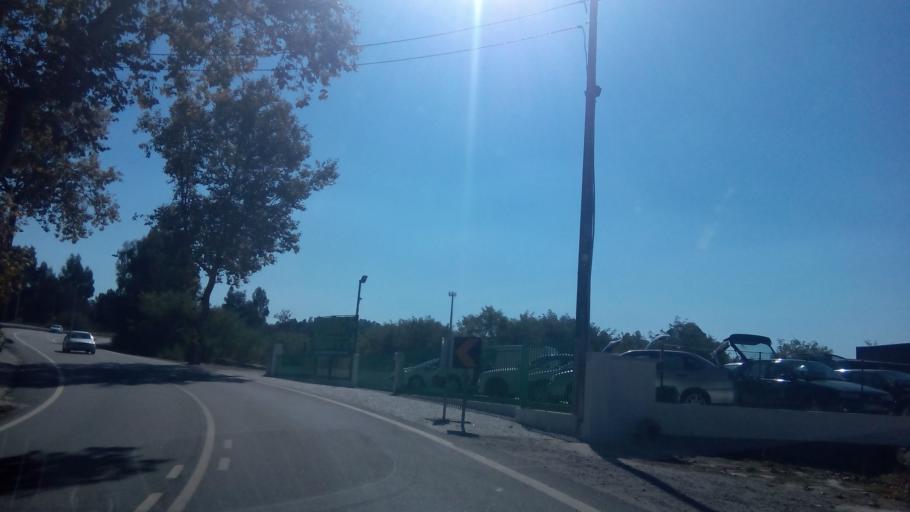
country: PT
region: Porto
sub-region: Lousada
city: Meinedo
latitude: 41.2504
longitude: -8.2163
